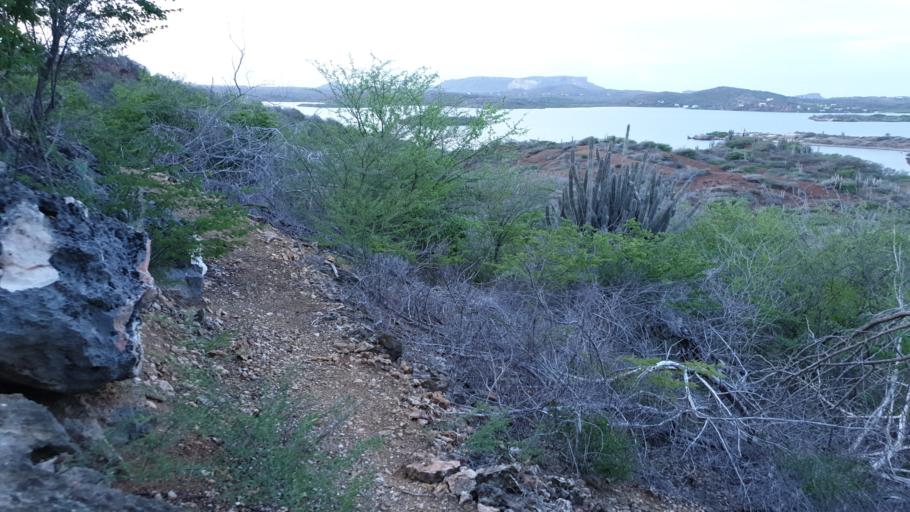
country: CW
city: Newport
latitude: 12.1299
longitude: -68.8148
